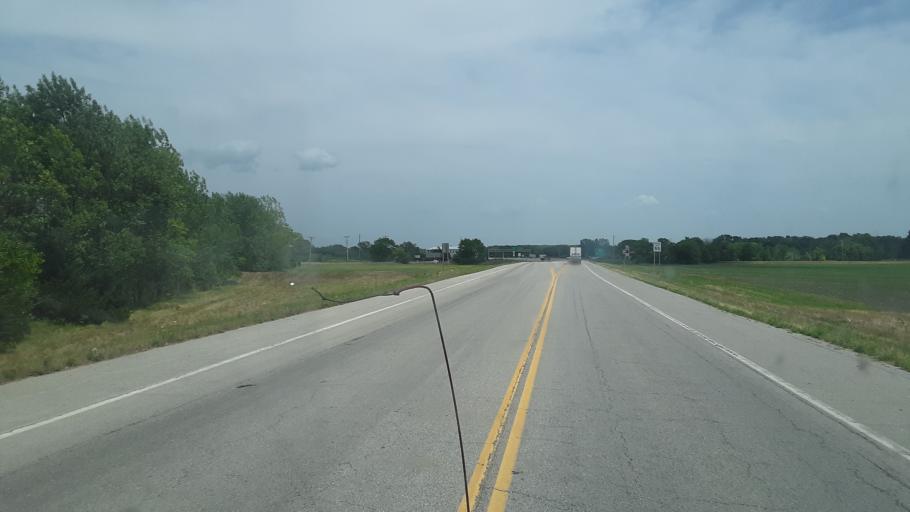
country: US
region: Kansas
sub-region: Bourbon County
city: Fort Scott
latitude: 37.8565
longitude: -94.7183
